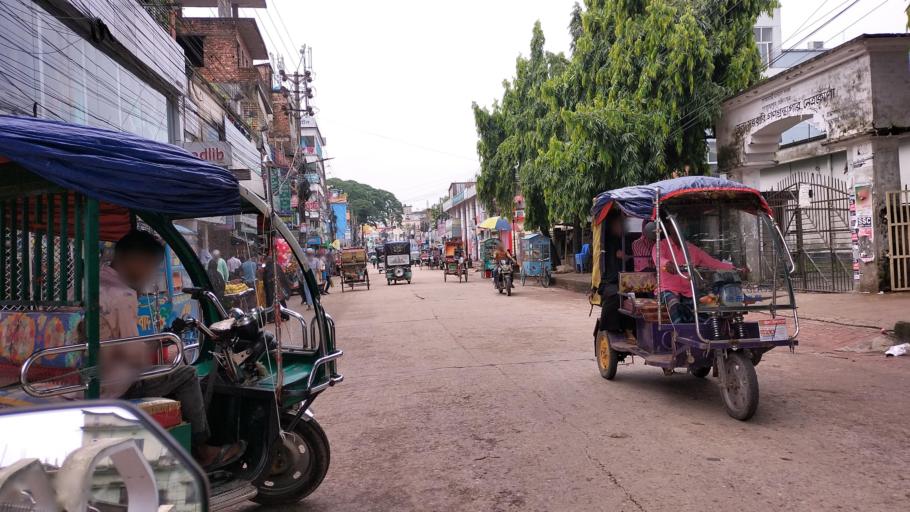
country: BD
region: Dhaka
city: Netrakona
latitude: 24.8789
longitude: 90.7311
